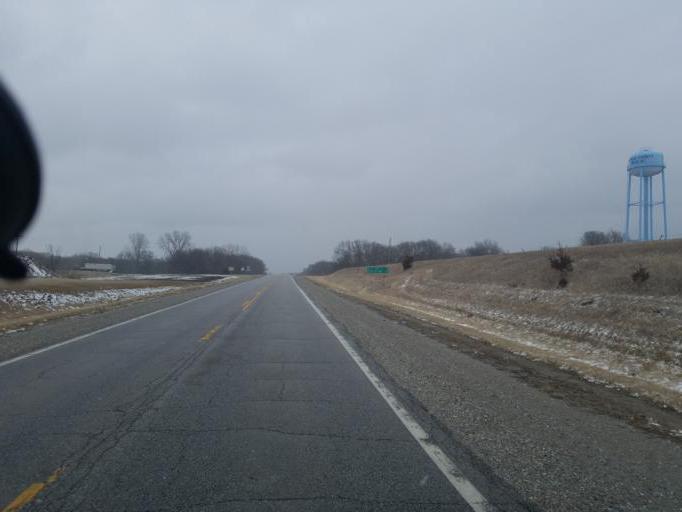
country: US
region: Missouri
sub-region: Putnam County
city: Unionville
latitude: 40.4715
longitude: -92.8133
